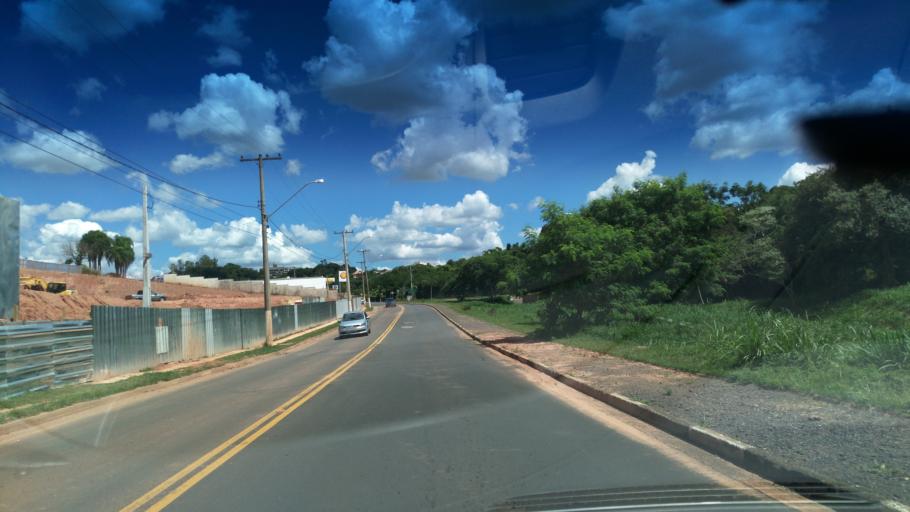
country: BR
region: Sao Paulo
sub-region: Valinhos
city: Valinhos
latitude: -22.9744
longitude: -47.0147
